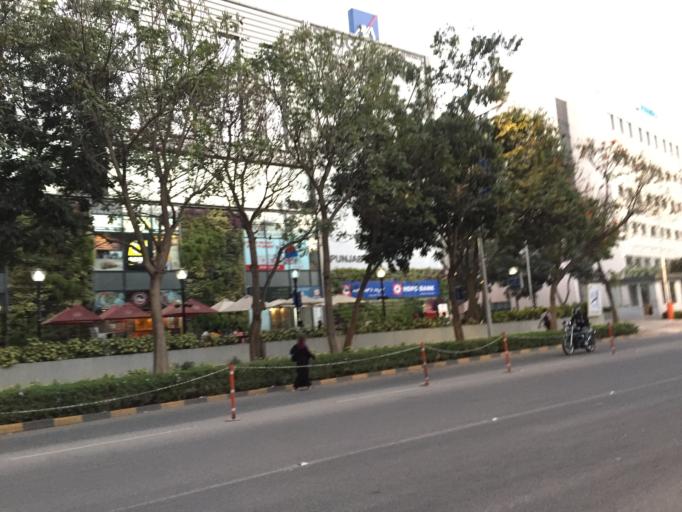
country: IN
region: Karnataka
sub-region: Bangalore Urban
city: Yelahanka
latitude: 13.0447
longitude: 77.6206
